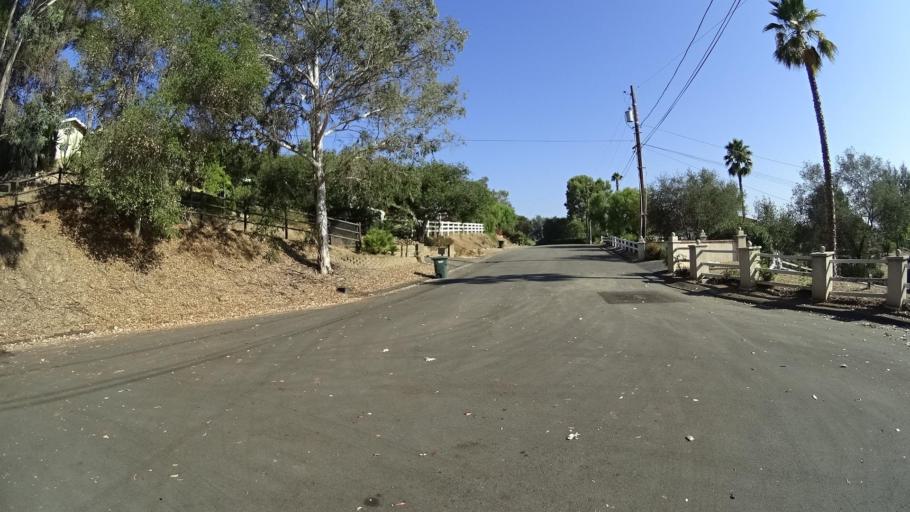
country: US
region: California
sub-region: San Diego County
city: Fallbrook
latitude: 33.3386
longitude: -117.2431
